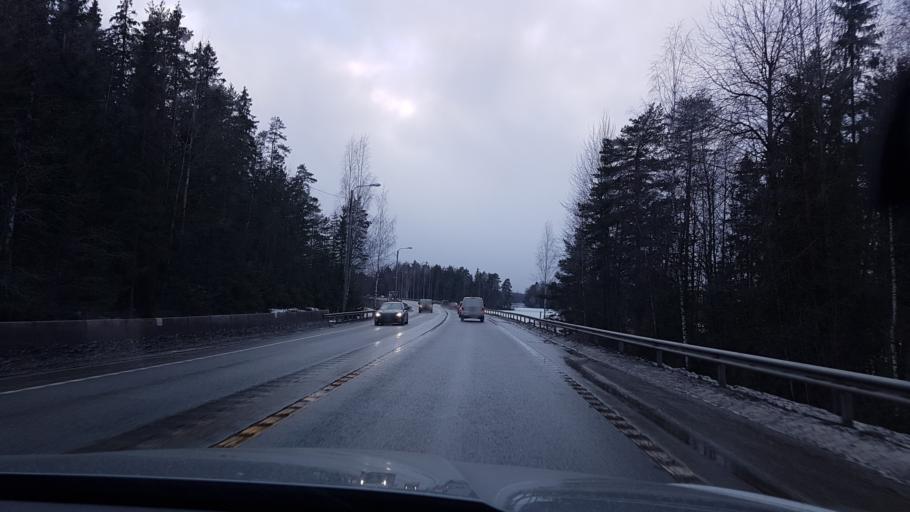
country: FI
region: Pirkanmaa
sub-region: Tampere
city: Kangasala
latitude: 61.5276
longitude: 23.9373
